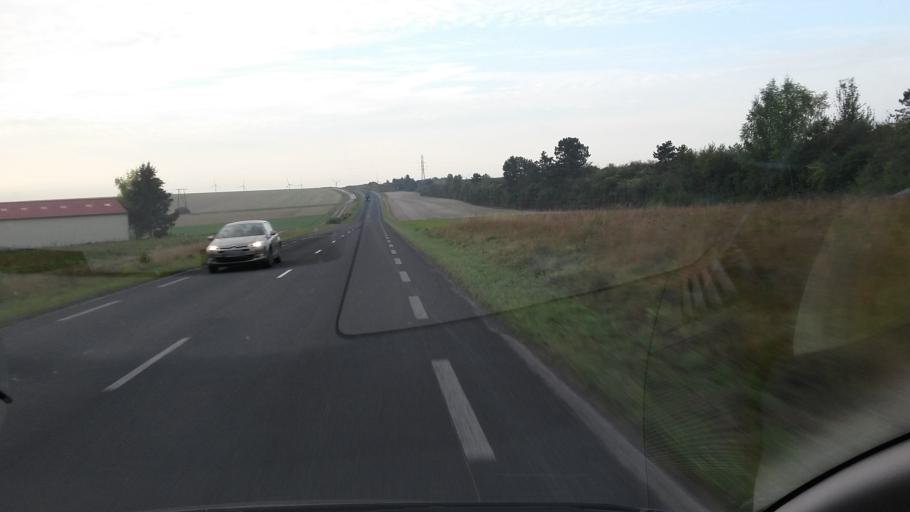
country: FR
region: Champagne-Ardenne
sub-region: Departement de la Marne
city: Fere-Champenoise
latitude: 48.7752
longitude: 3.9940
